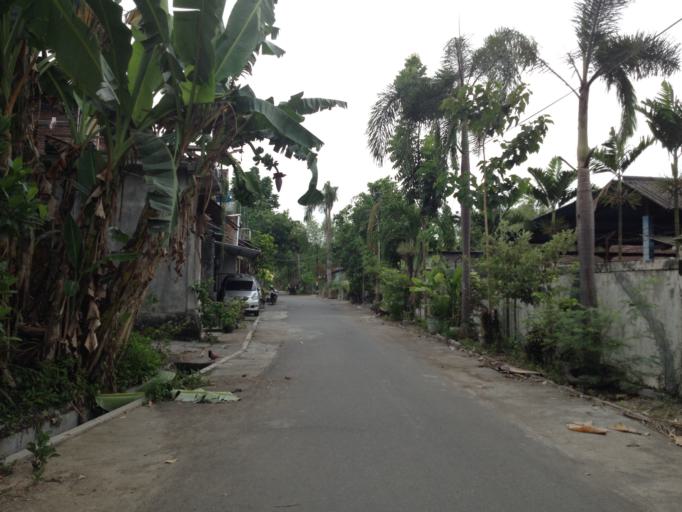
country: ID
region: Daerah Istimewa Yogyakarta
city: Yogyakarta
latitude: -7.8277
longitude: 110.3860
